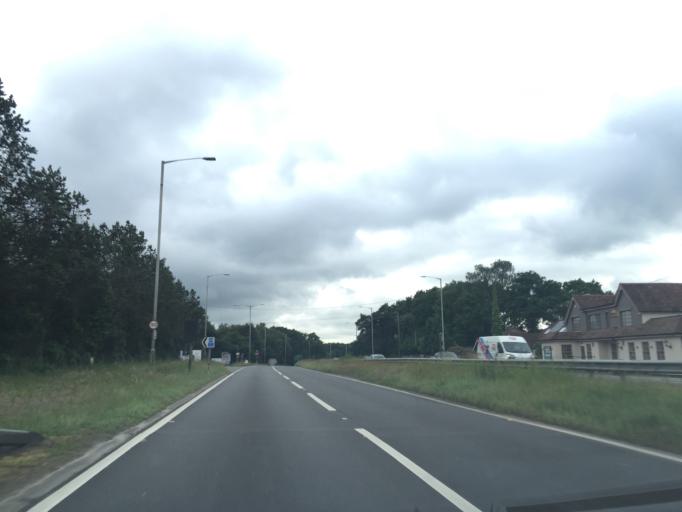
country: GB
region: England
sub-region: Dorset
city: St Leonards
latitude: 50.8188
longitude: -1.8577
